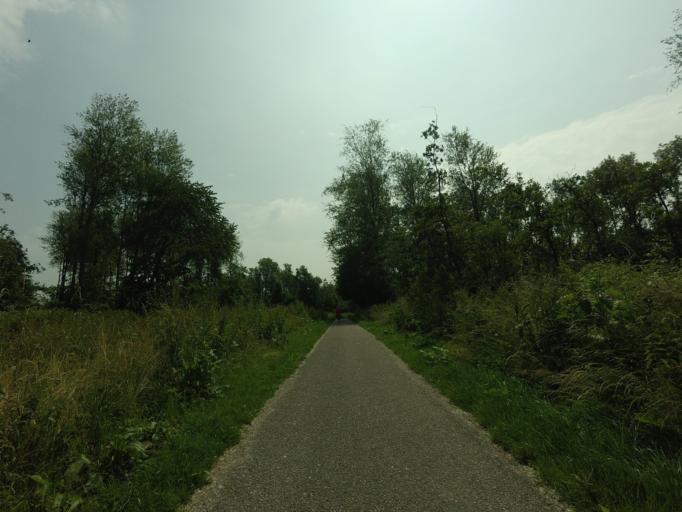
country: NL
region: South Holland
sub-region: Gemeente Krimpen aan den IJssel
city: Krimpen aan den IJssel
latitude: 51.9622
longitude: 4.6324
